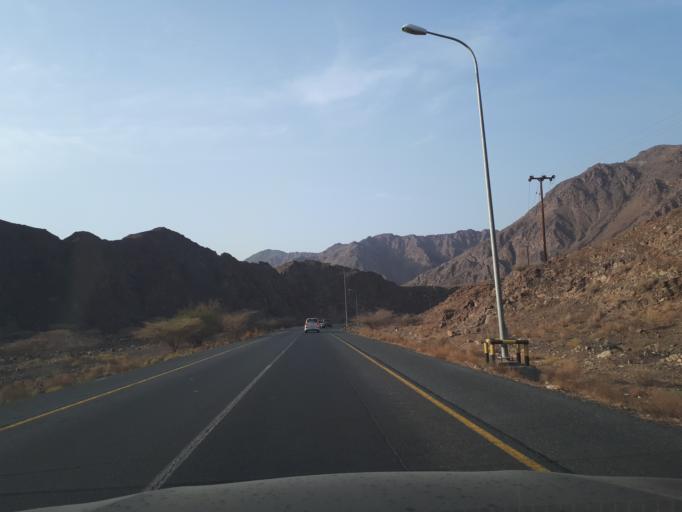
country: OM
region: Muhafazat ad Dakhiliyah
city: Sufalat Sama'il
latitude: 23.1751
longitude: 58.0955
